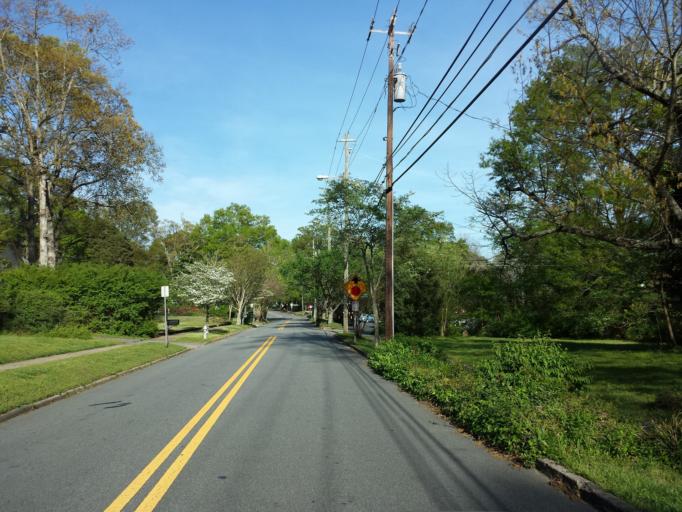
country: US
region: Georgia
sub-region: Cobb County
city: Marietta
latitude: 33.9576
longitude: -84.5583
